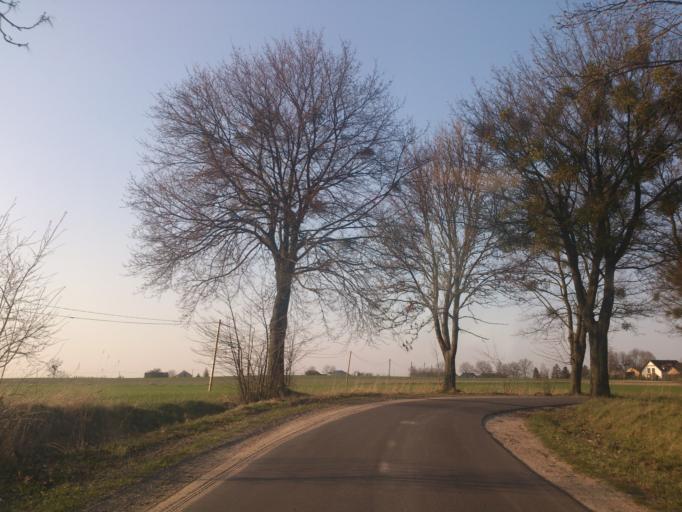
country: PL
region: Kujawsko-Pomorskie
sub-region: Powiat golubsko-dobrzynski
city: Radomin
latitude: 53.1169
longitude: 19.1367
